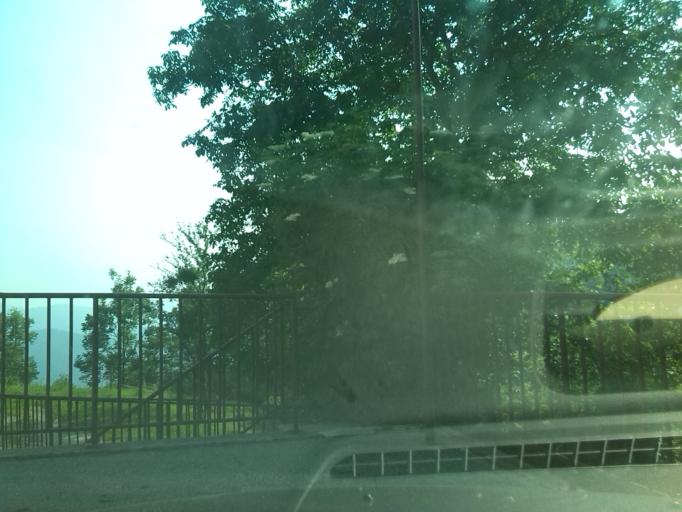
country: IT
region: Friuli Venezia Giulia
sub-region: Provincia di Udine
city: Cras
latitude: 46.1925
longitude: 13.6183
